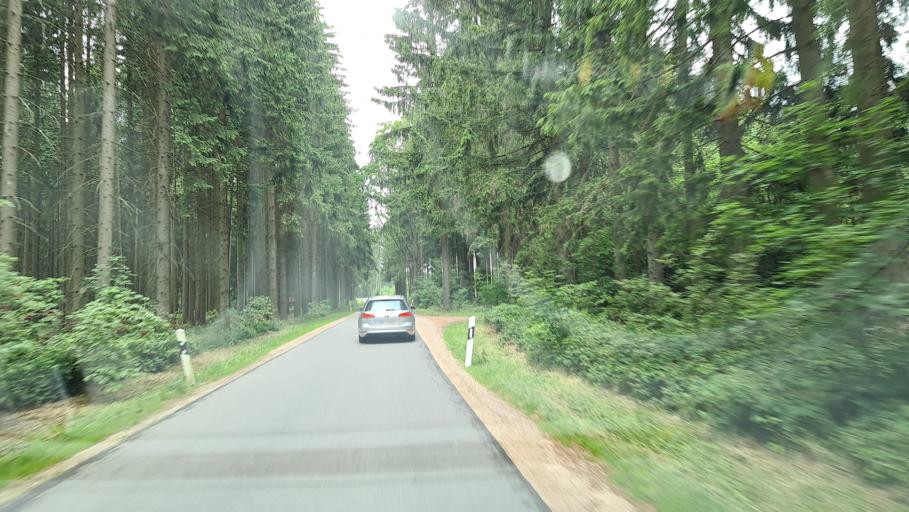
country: DE
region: Saxony
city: Stutzengrun
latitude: 50.5433
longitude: 12.4826
